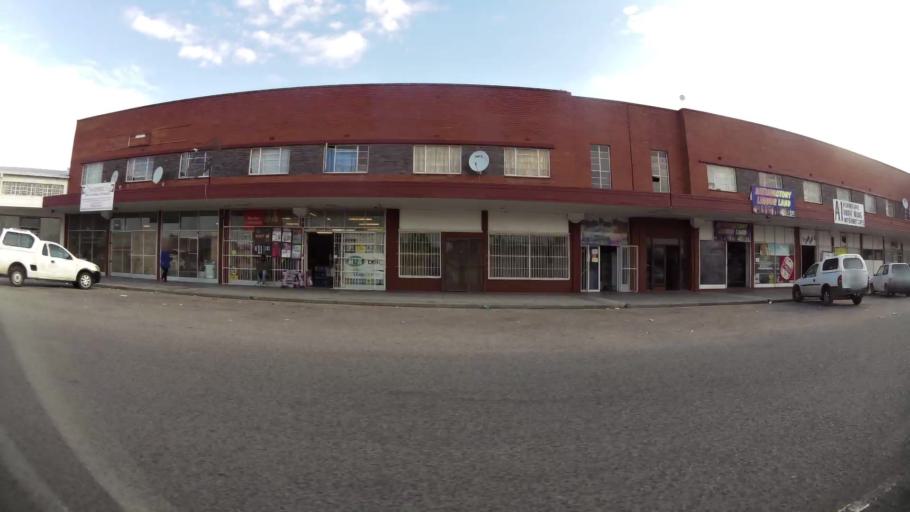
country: ZA
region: Orange Free State
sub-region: Lejweleputswa District Municipality
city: Welkom
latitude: -27.9905
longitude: 26.7116
